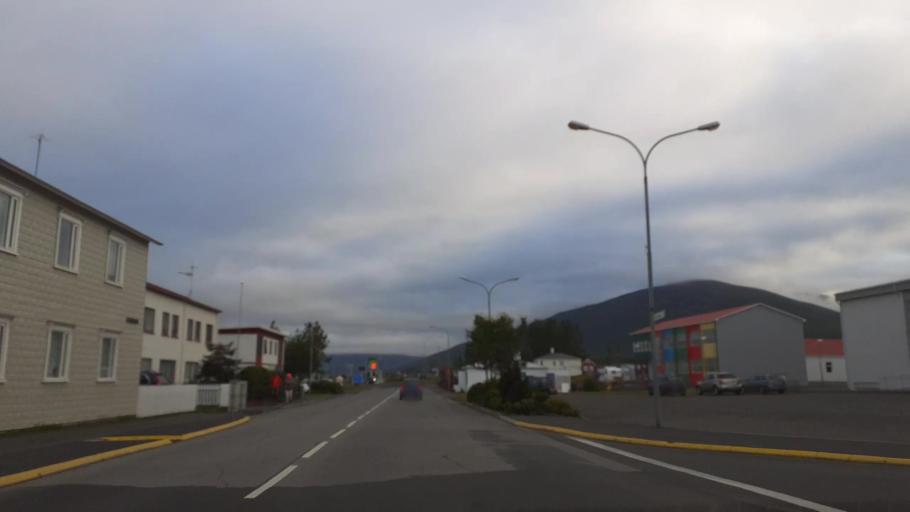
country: IS
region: Northeast
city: Dalvik
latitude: 65.9688
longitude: -18.5282
